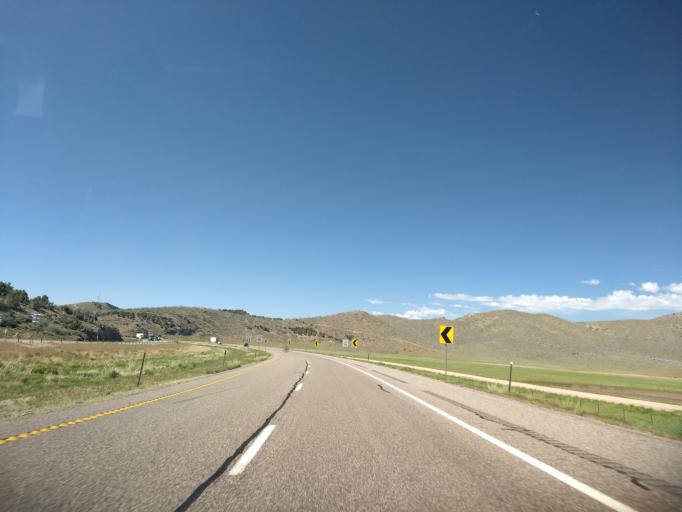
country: US
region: Utah
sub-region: Beaver County
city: Beaver
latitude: 38.6680
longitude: -112.5883
